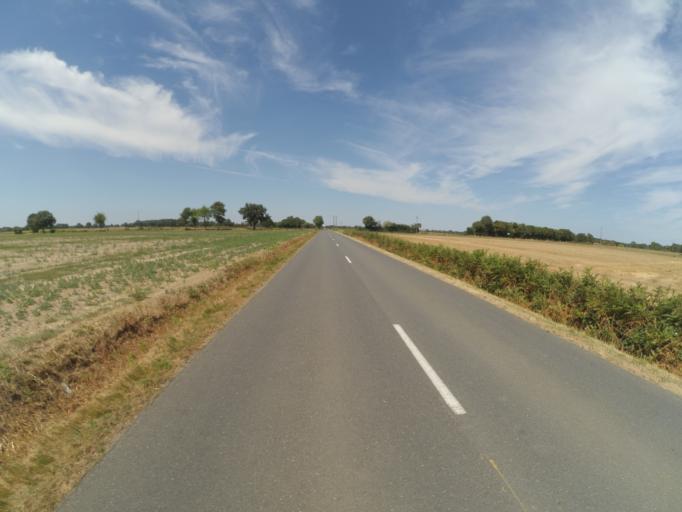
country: FR
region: Poitou-Charentes
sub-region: Departement de la Vienne
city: Usson-du-Poitou
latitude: 46.1839
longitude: 0.5414
